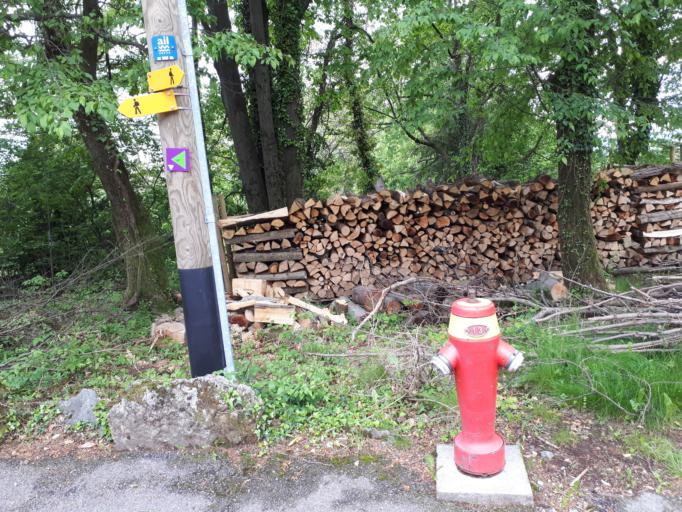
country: CH
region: Ticino
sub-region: Mendrisio District
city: Castel San Pietro
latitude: 45.8652
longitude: 9.0045
